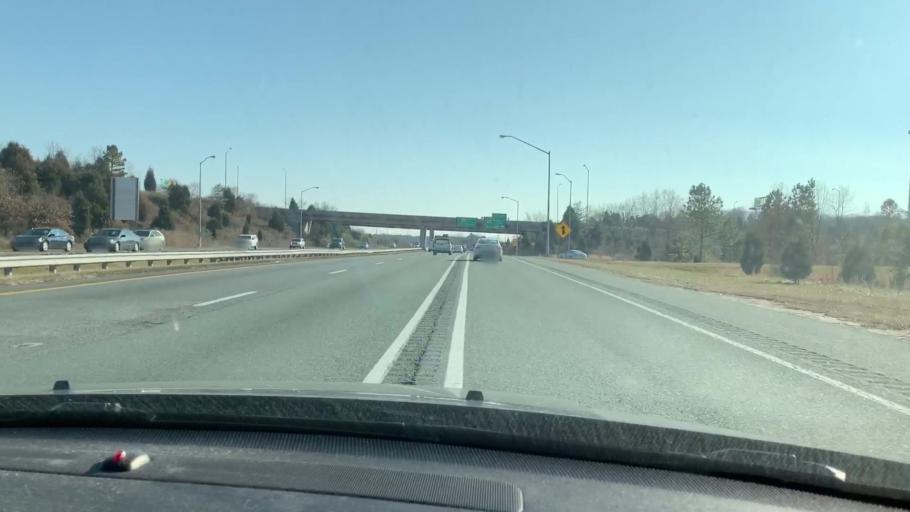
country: US
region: Maryland
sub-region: Howard County
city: Hanover
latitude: 39.1715
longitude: -76.7331
